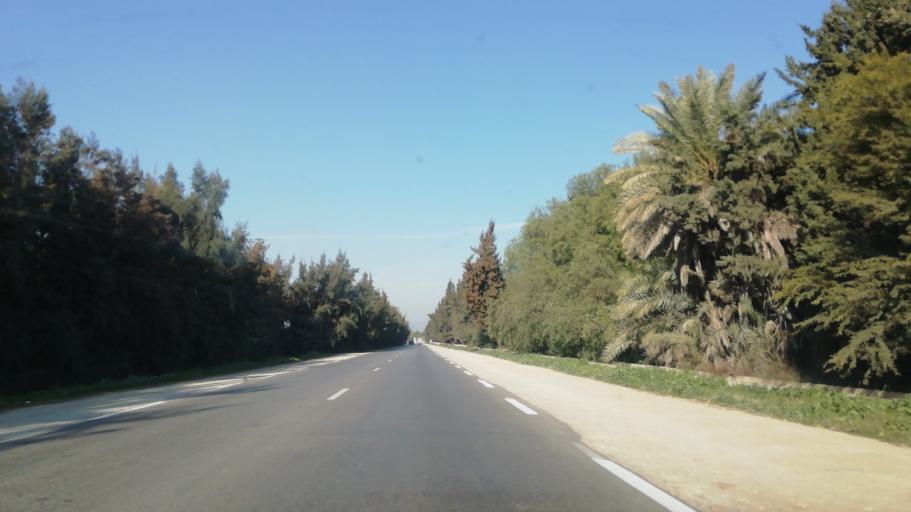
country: DZ
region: Relizane
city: Relizane
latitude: 35.7300
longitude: 0.4740
